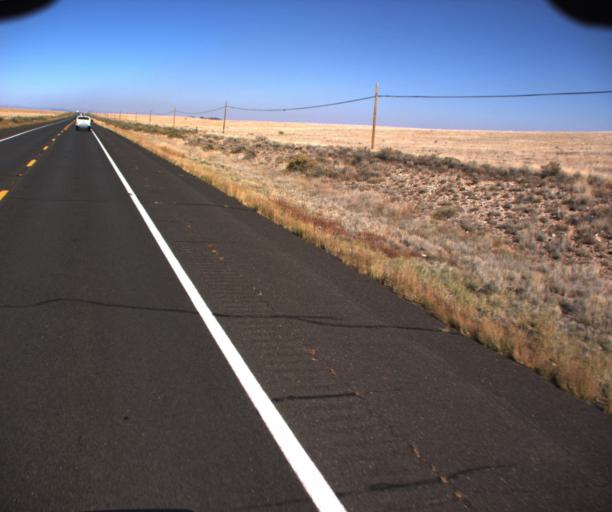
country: US
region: Arizona
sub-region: Coconino County
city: Flagstaff
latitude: 35.6098
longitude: -111.5240
